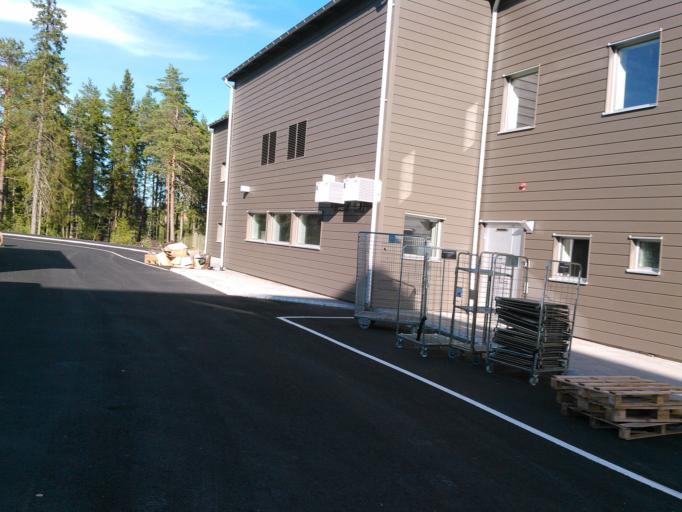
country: SE
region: Vaesterbotten
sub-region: Umea Kommun
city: Umea
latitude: 63.8229
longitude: 20.3198
